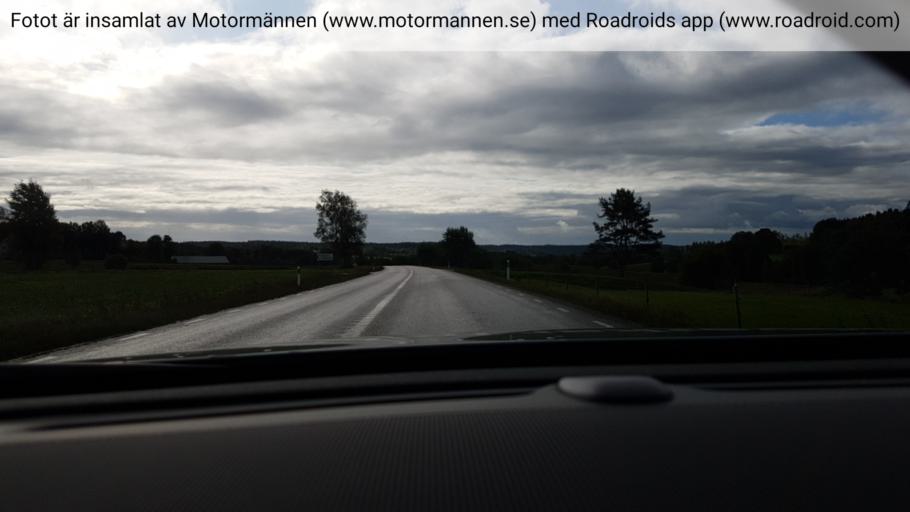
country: SE
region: Vaestra Goetaland
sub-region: Harryda Kommun
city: Ravlanda
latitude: 57.5306
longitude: 12.5352
